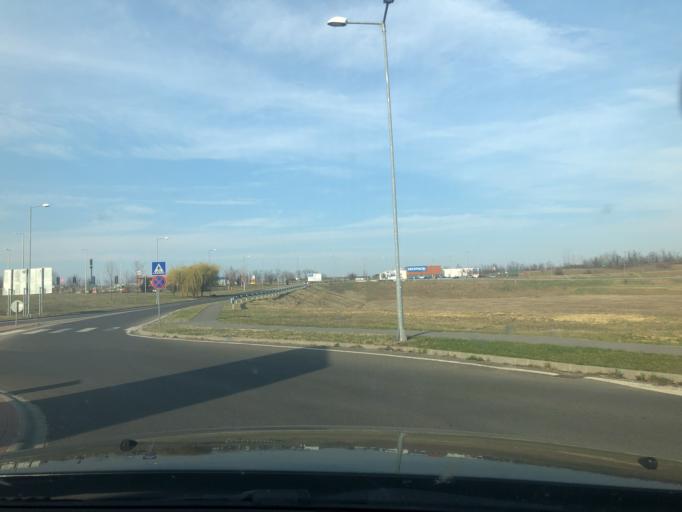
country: HU
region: Pest
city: Ecser
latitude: 47.4588
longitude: 19.3348
